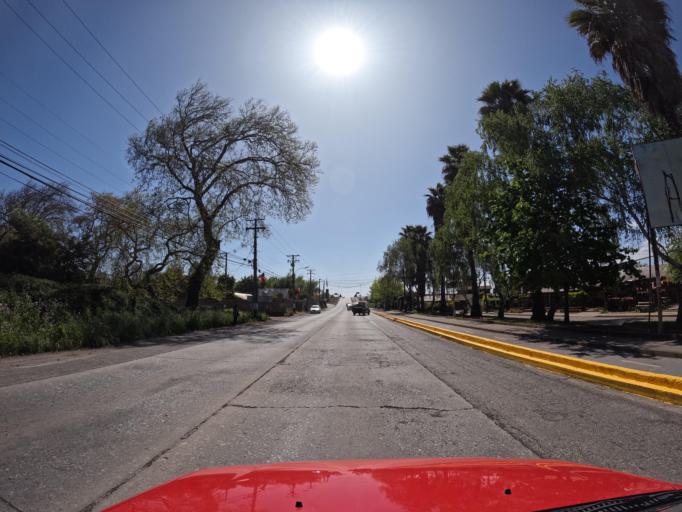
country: CL
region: Maule
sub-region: Provincia de Curico
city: Molina
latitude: -35.0515
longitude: -71.2793
